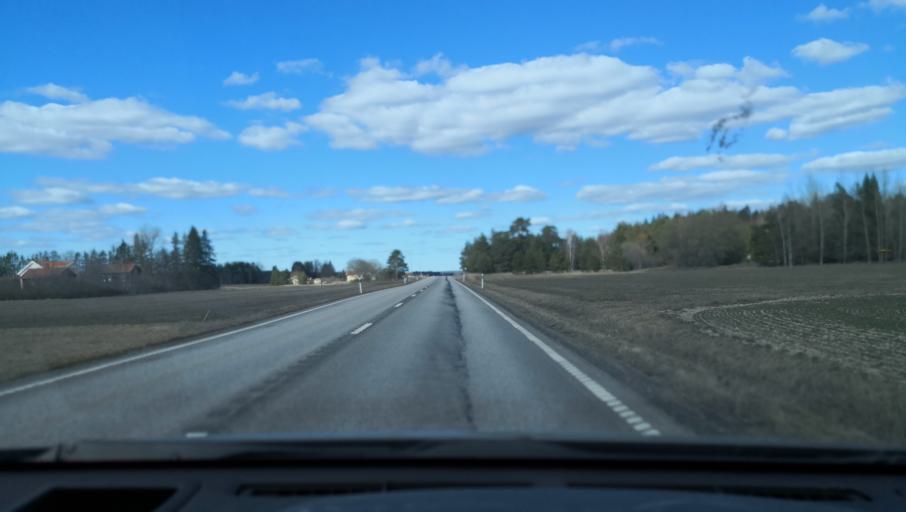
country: SE
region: Vaestmanland
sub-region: Sala Kommun
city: Sala
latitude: 59.8704
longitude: 16.6280
